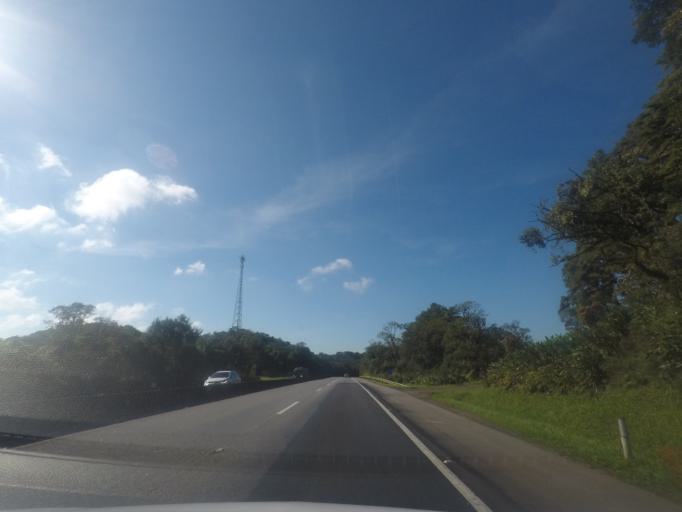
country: BR
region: Parana
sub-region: Piraquara
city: Piraquara
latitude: -25.5814
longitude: -48.9624
